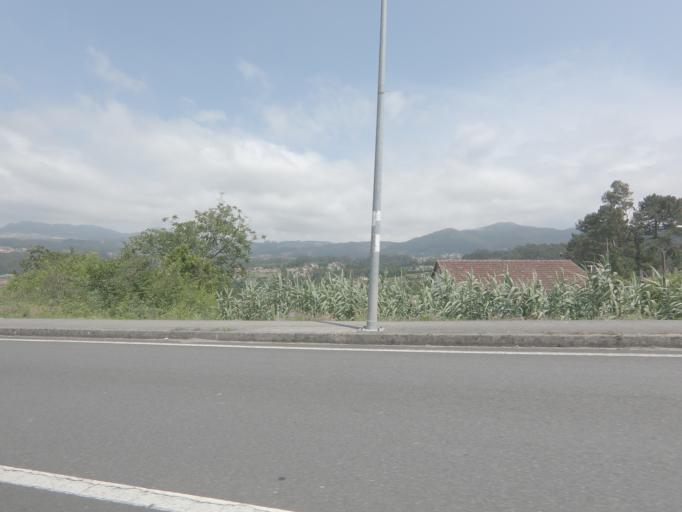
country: ES
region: Galicia
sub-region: Provincia de Pontevedra
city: Gondomar
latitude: 42.1005
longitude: -8.7590
